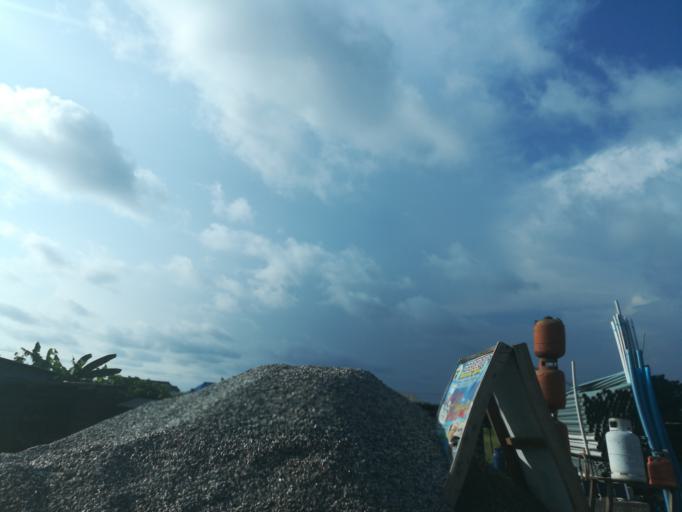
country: NG
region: Ogun
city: Ado Odo
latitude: 6.4885
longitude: 3.0711
